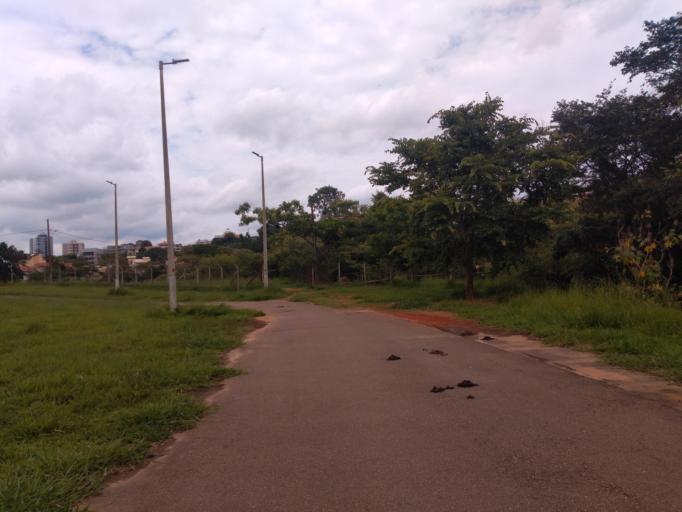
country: BR
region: Minas Gerais
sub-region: Tres Coracoes
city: Tres Coracoes
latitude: -21.6996
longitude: -45.2471
